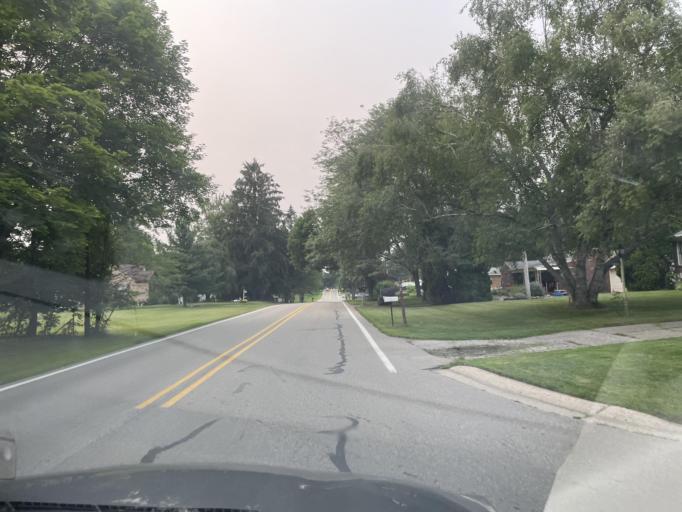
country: US
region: Michigan
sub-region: Kent County
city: Walker
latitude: 42.9673
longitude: -85.7370
